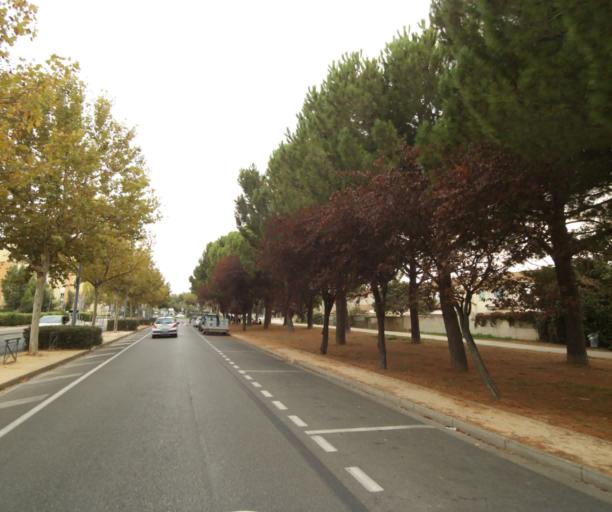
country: FR
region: Provence-Alpes-Cote d'Azur
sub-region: Departement des Bouches-du-Rhone
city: Marignane
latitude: 43.4129
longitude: 5.2048
